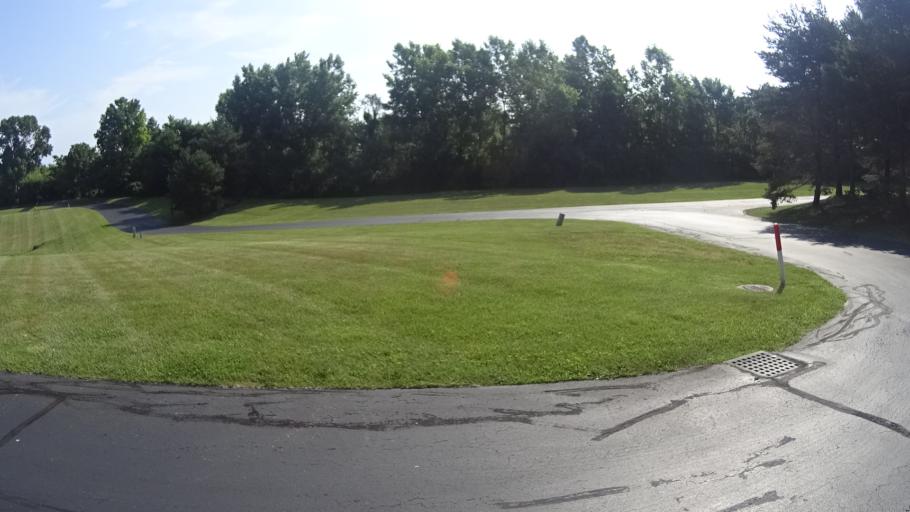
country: US
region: Ohio
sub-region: Lorain County
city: Vermilion
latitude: 41.3922
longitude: -82.4365
